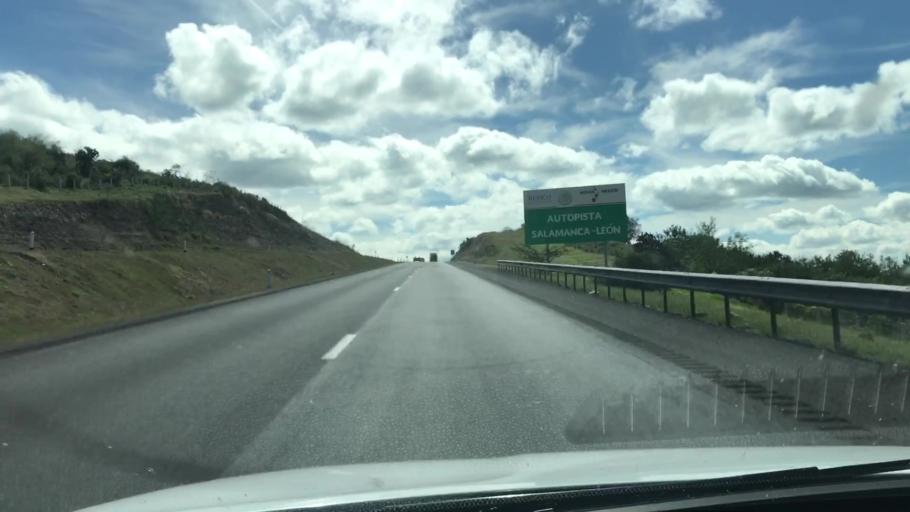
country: MX
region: Guanajuato
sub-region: Irapuato
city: Ex-Hacienda del Copal
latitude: 20.7387
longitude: -101.3063
